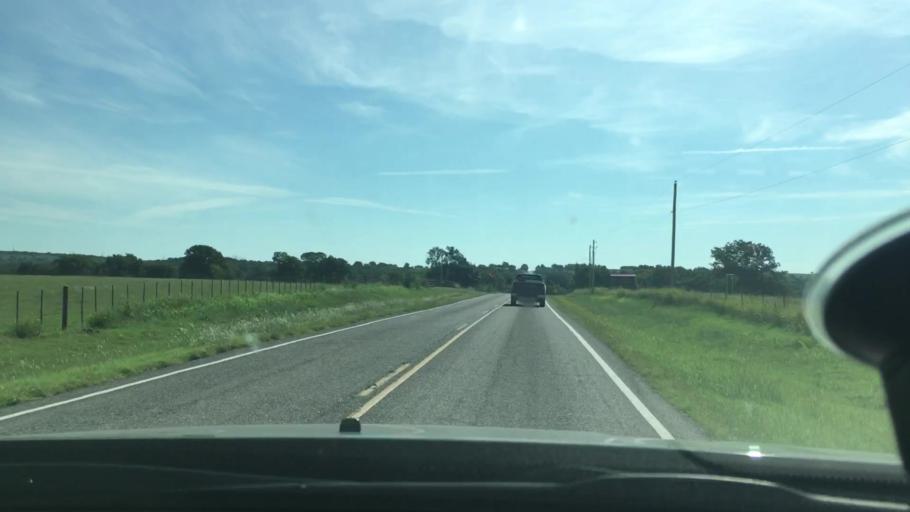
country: US
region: Oklahoma
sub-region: Carter County
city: Lone Grove
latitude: 34.3327
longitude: -97.2405
